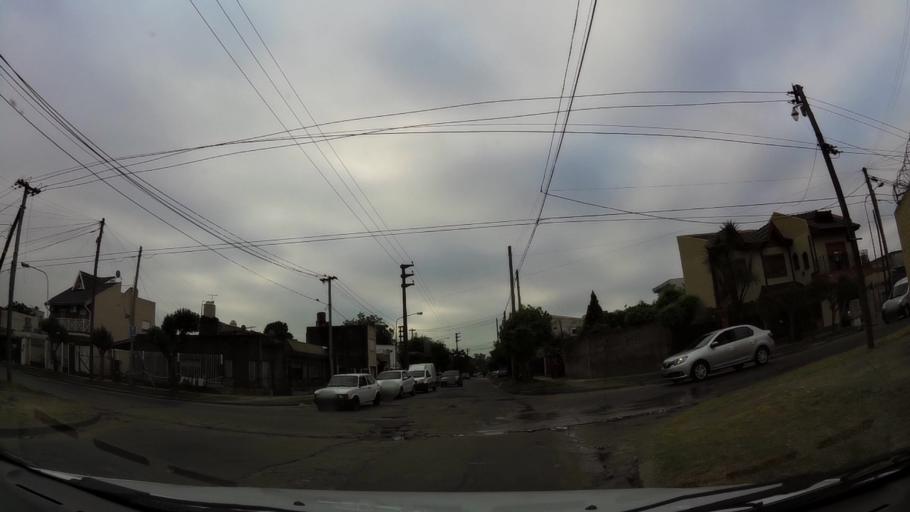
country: AR
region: Buenos Aires
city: San Justo
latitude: -34.6866
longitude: -58.5914
